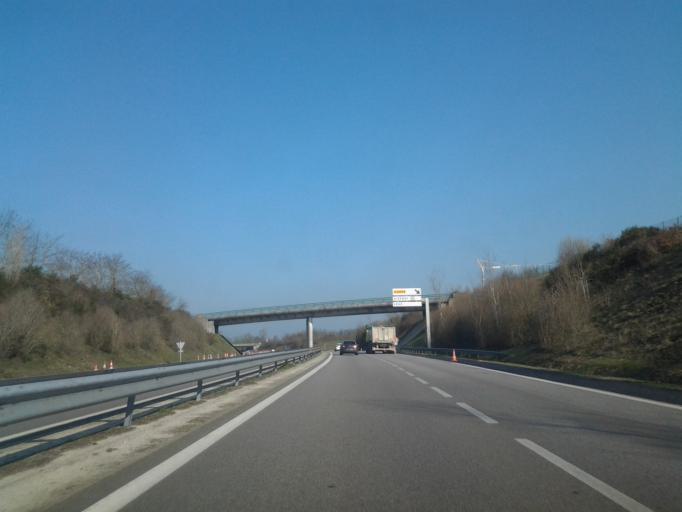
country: FR
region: Pays de la Loire
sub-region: Departement de la Vendee
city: Aizenay
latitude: 46.7431
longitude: -1.6215
